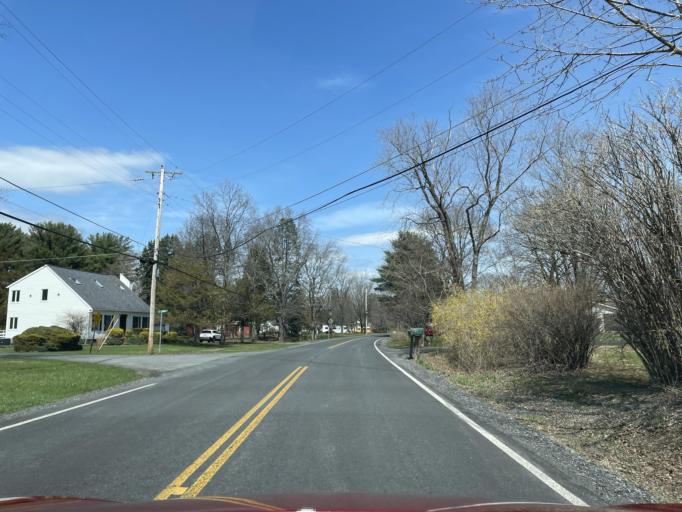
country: US
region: New York
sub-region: Ulster County
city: Manorville
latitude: 42.1284
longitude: -74.0198
